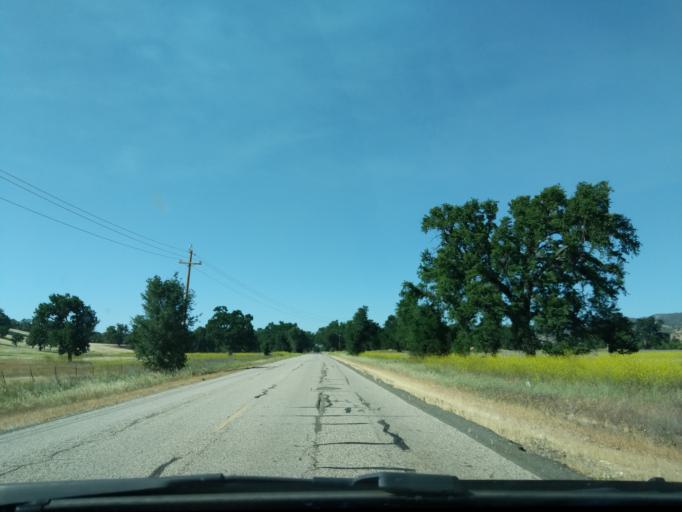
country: US
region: California
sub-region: Monterey County
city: King City
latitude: 36.0140
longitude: -121.1792
